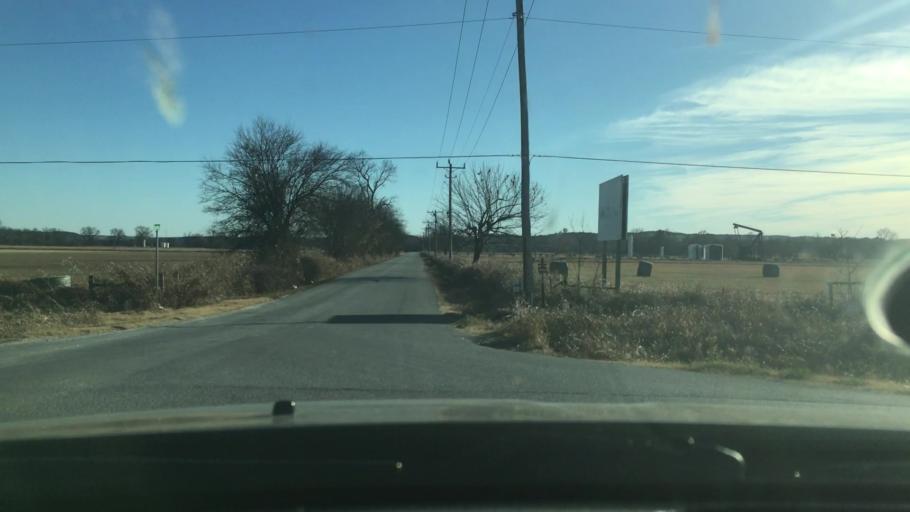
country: US
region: Oklahoma
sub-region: Murray County
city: Davis
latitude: 34.5064
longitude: -97.1560
